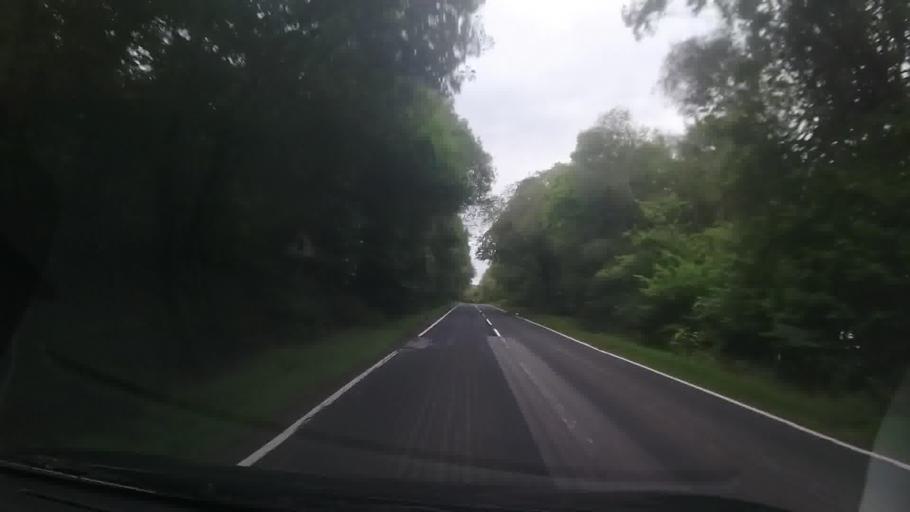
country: GB
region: Scotland
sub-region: Argyll and Bute
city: Garelochhead
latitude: 56.2113
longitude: -5.0530
